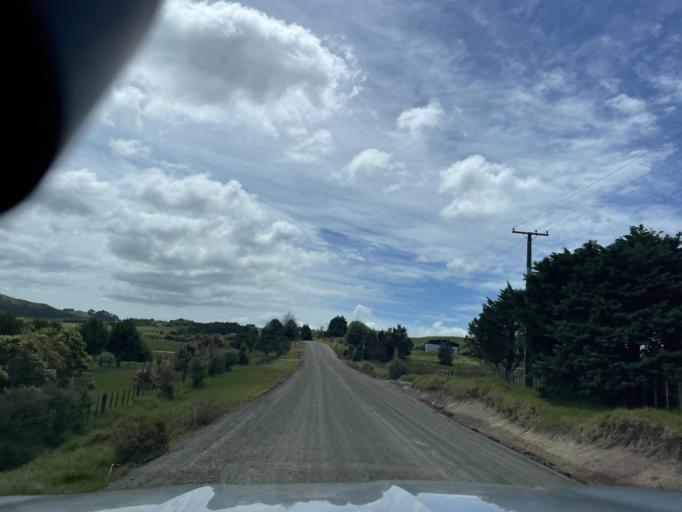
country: NZ
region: Auckland
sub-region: Auckland
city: Wellsford
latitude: -36.1699
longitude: 174.2766
